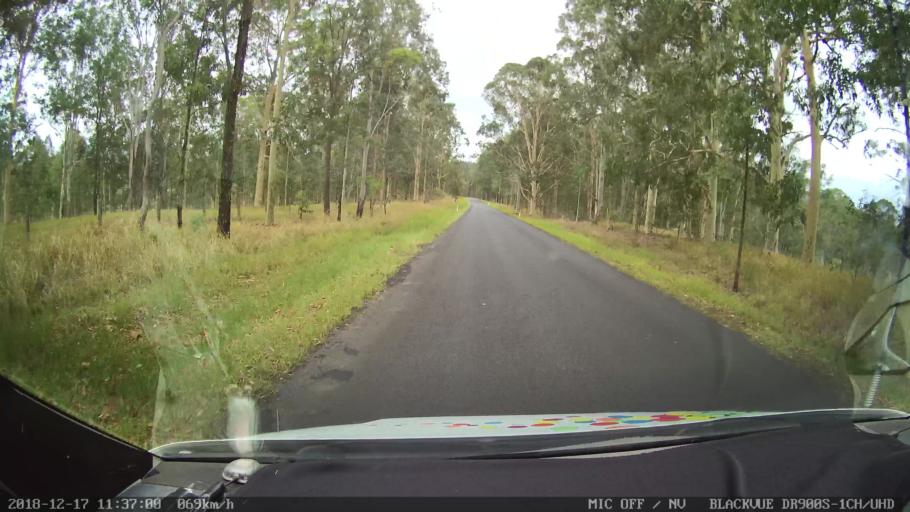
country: AU
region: New South Wales
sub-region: Kyogle
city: Kyogle
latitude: -28.7086
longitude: 152.6061
